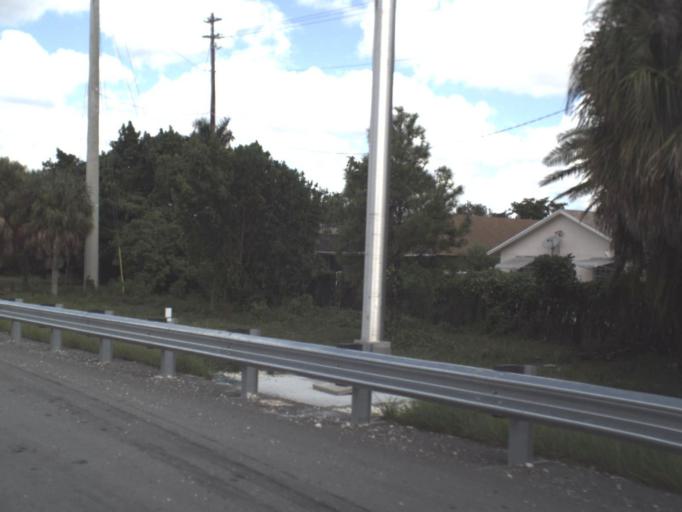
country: US
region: Florida
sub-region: Broward County
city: Miramar
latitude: 25.9765
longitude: -80.2287
